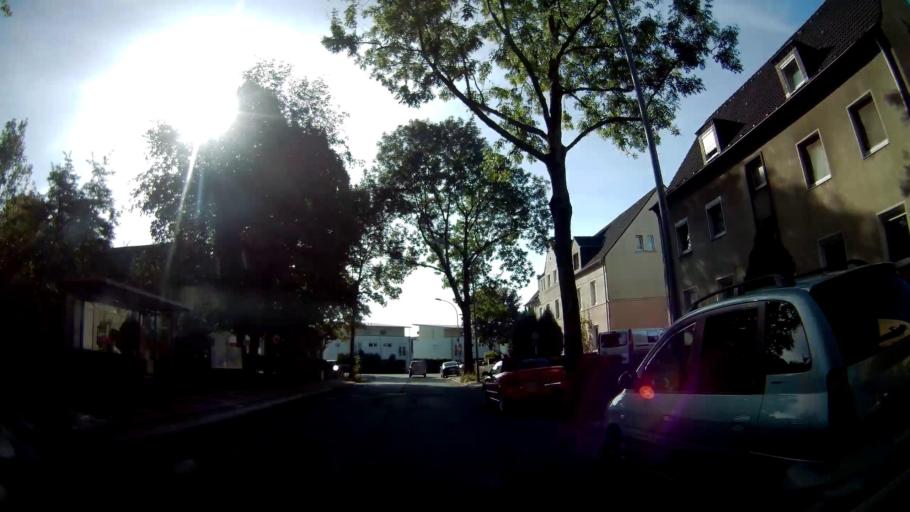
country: DE
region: North Rhine-Westphalia
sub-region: Regierungsbezirk Arnsberg
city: Herne
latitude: 51.5127
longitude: 7.2525
